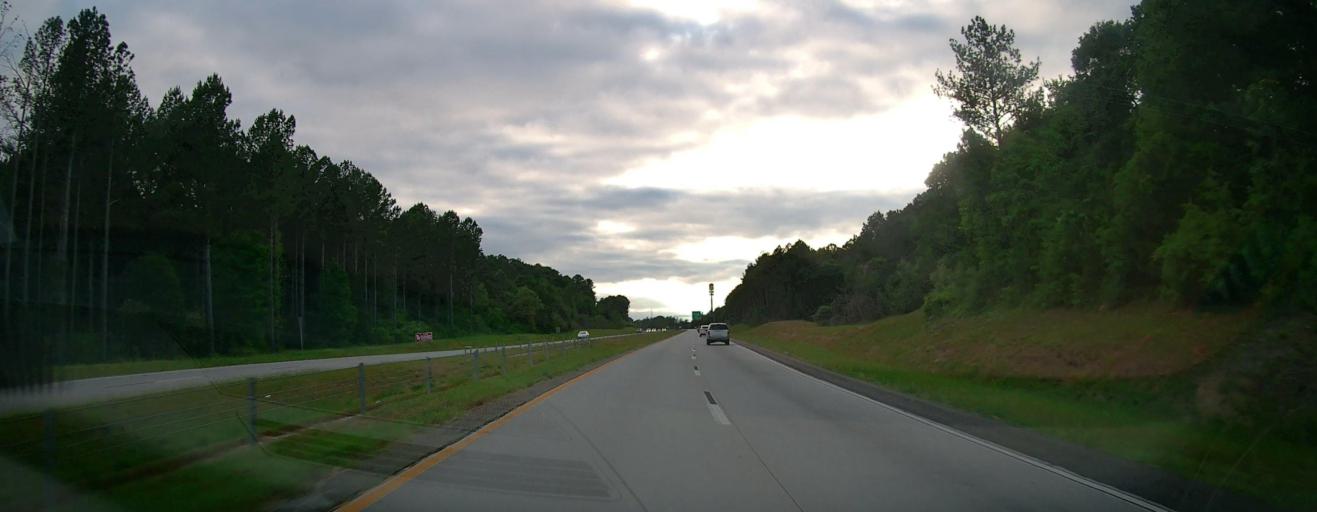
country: US
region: Georgia
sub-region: Oconee County
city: Watkinsville
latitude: 33.9094
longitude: -83.4395
